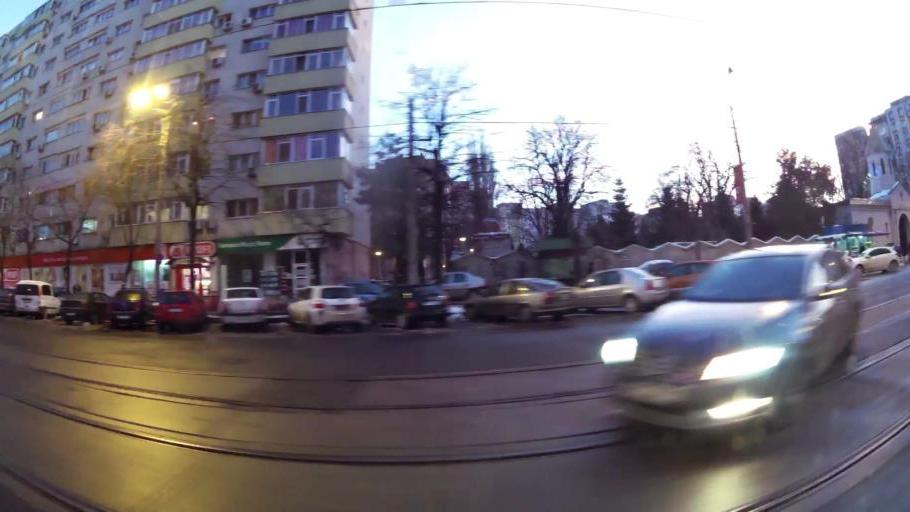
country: RO
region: Ilfov
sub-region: Comuna Fundeni-Dobroesti
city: Fundeni
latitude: 44.4444
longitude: 26.1414
